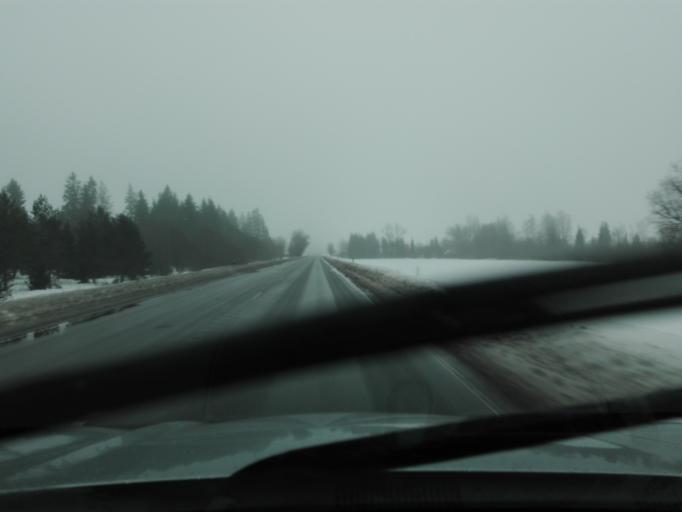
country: EE
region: Raplamaa
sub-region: Kohila vald
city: Kohila
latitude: 59.2050
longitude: 24.7811
